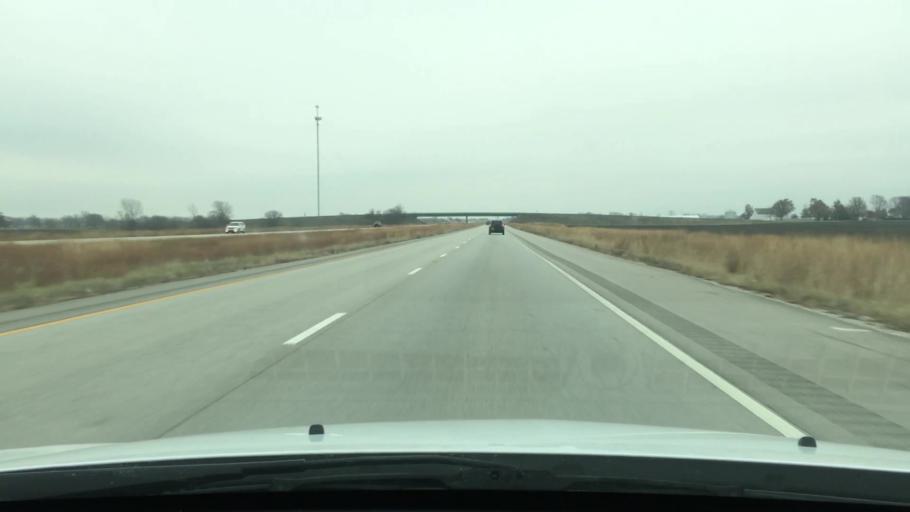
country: US
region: Illinois
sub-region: Morgan County
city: Jacksonville
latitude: 39.7380
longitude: -90.0861
